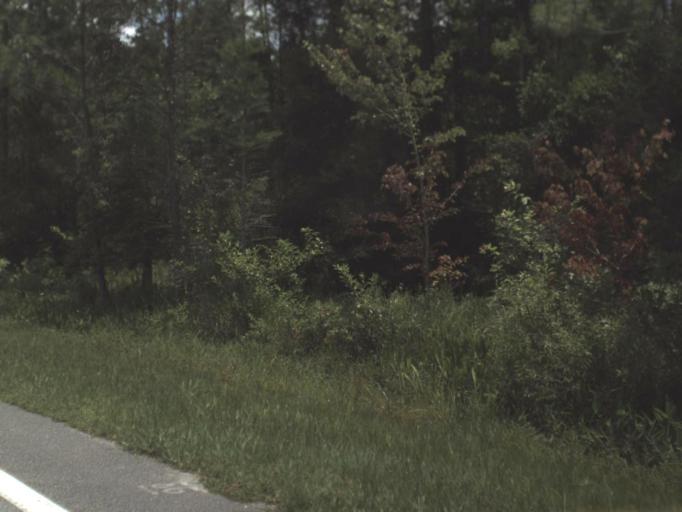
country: US
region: Florida
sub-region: Levy County
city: Bronson
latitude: 29.3781
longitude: -82.7136
